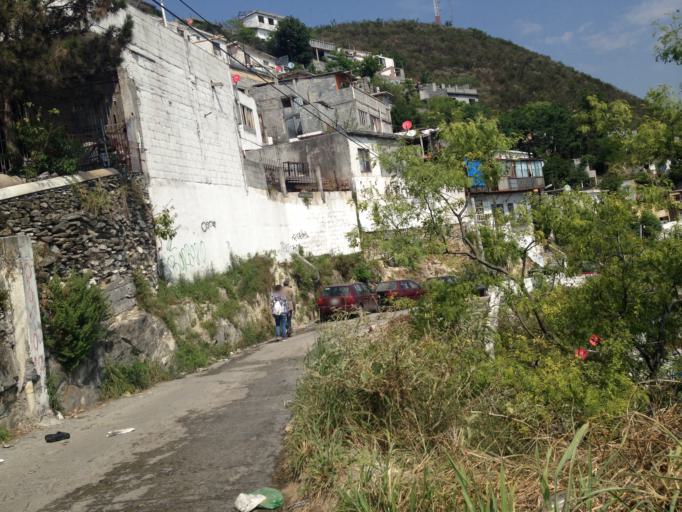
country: MX
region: Nuevo Leon
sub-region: Monterrey
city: Monterrey
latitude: 25.6548
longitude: -100.3299
